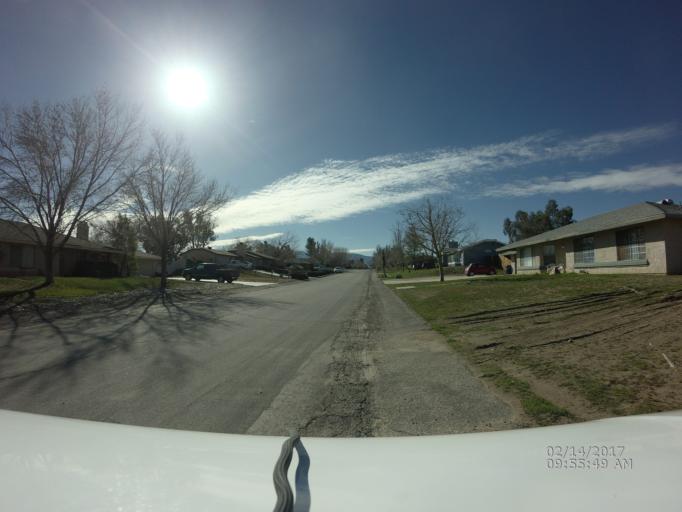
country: US
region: California
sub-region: Los Angeles County
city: Littlerock
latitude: 34.5557
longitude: -117.9614
